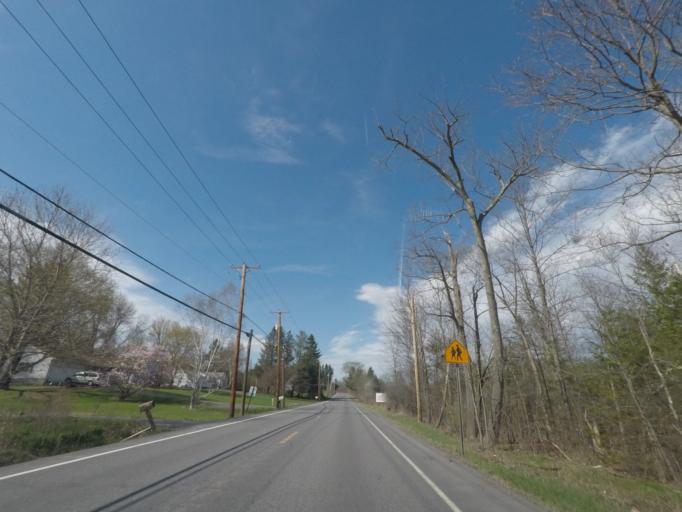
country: US
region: New York
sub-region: Greene County
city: Cairo
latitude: 42.4303
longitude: -74.0171
